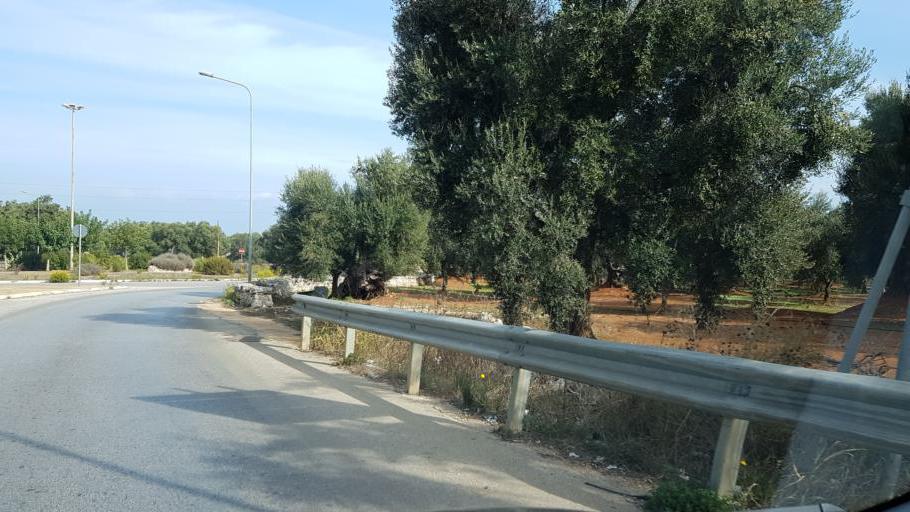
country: IT
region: Apulia
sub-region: Provincia di Brindisi
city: Ostuni
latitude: 40.7437
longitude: 17.5794
